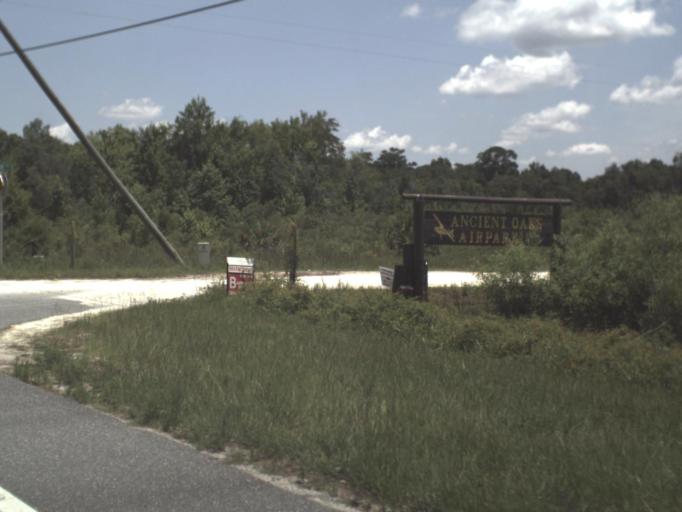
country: US
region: Florida
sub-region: Taylor County
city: Steinhatchee
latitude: 29.7201
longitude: -83.3600
